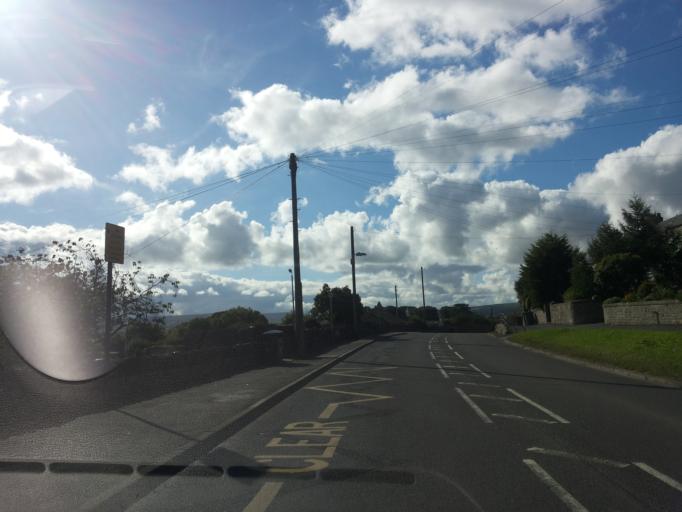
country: GB
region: England
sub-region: North Yorkshire
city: Leyburn
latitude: 54.3139
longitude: -1.8243
